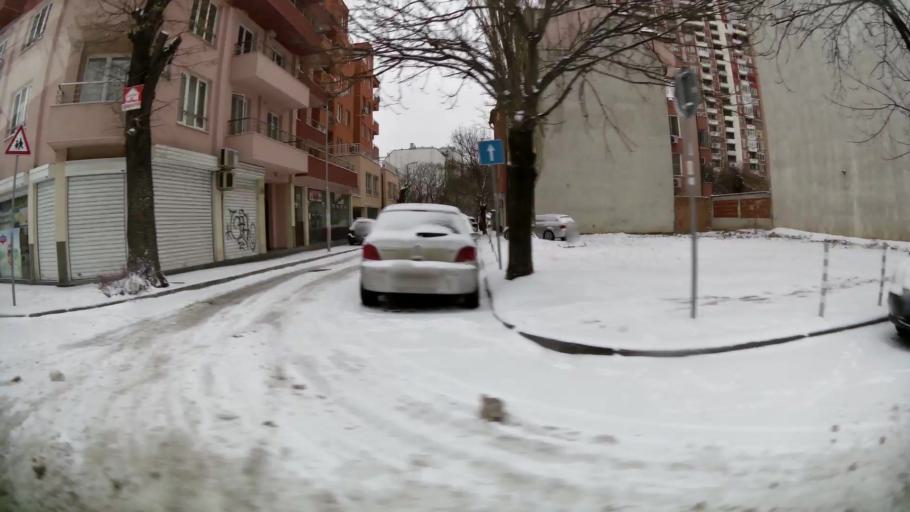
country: BG
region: Sofia-Capital
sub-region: Stolichna Obshtina
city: Sofia
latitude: 42.6990
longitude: 23.3002
